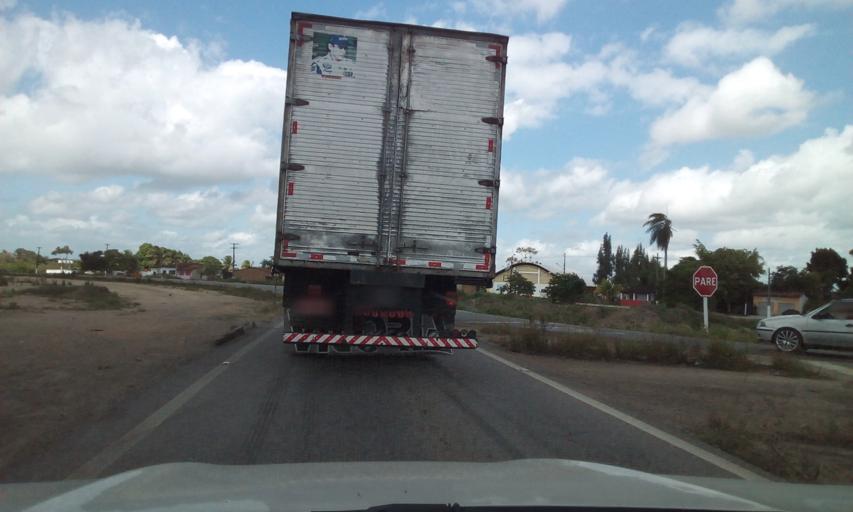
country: BR
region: Alagoas
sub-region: Pilar
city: Pilar
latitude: -9.5667
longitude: -35.9693
